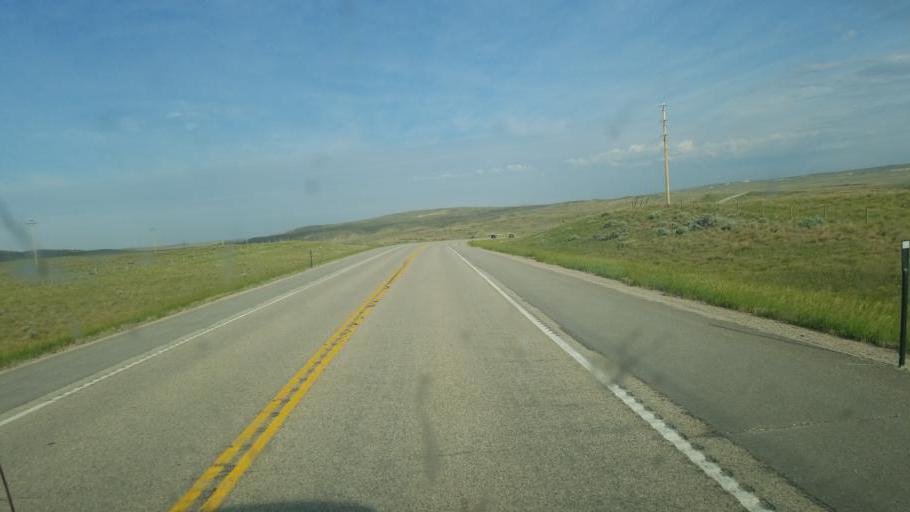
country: US
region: Wyoming
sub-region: Natrona County
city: Mills
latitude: 43.0336
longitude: -107.0115
